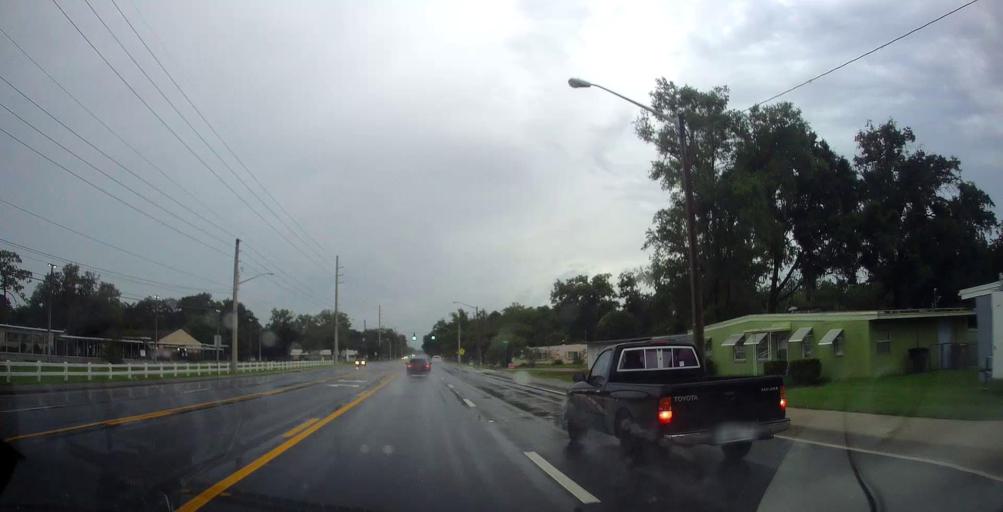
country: US
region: Florida
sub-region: Marion County
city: Ocala
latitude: 29.1819
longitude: -82.0869
